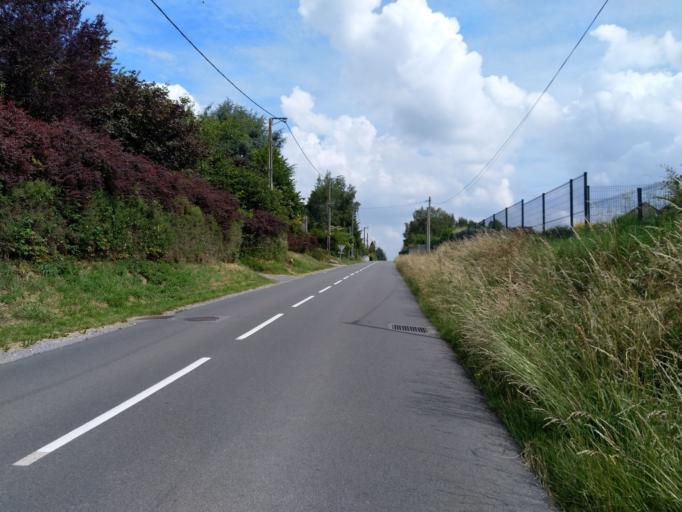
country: FR
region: Nord-Pas-de-Calais
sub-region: Departement du Nord
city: Rousies
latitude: 50.3035
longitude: 3.9960
